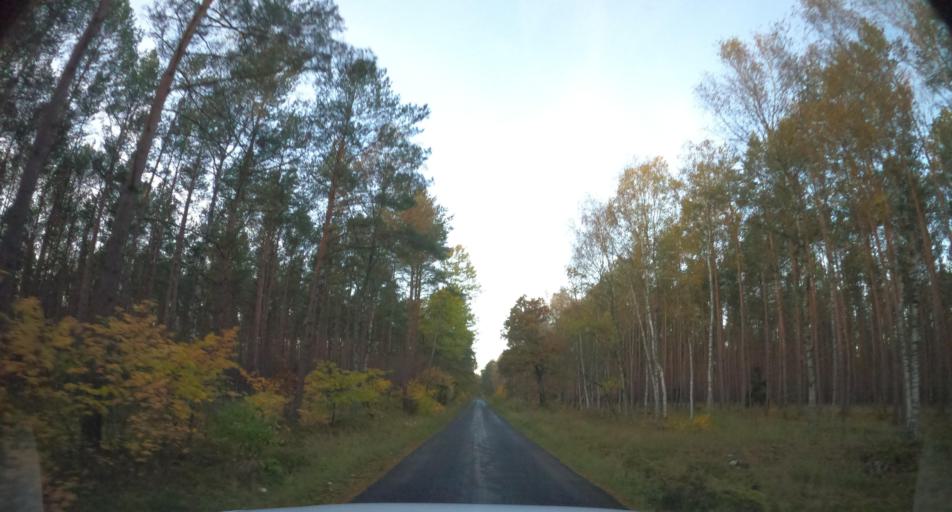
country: PL
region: West Pomeranian Voivodeship
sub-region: Powiat policki
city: Nowe Warpno
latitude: 53.6449
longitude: 14.4235
